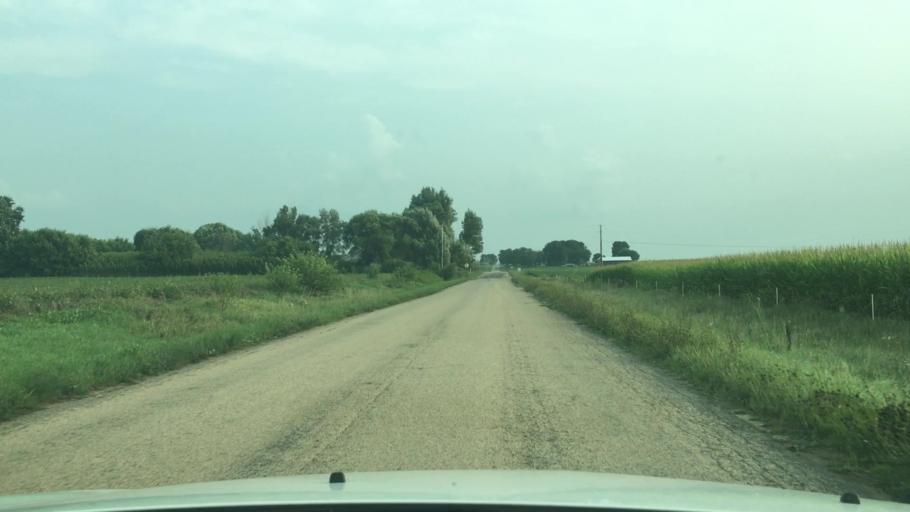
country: US
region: Illinois
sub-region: Ogle County
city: Rochelle
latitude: 41.9218
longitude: -88.9806
